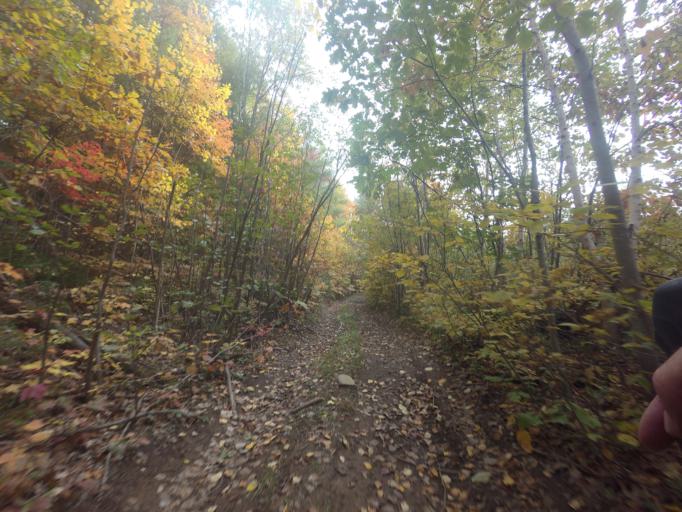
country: CA
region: Ontario
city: Pembroke
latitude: 45.7213
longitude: -77.2234
